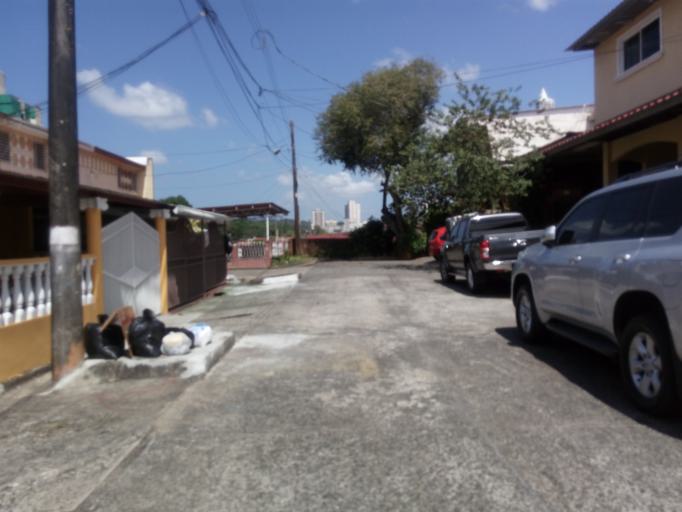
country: PA
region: Panama
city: Panama
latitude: 8.9952
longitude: -79.5388
